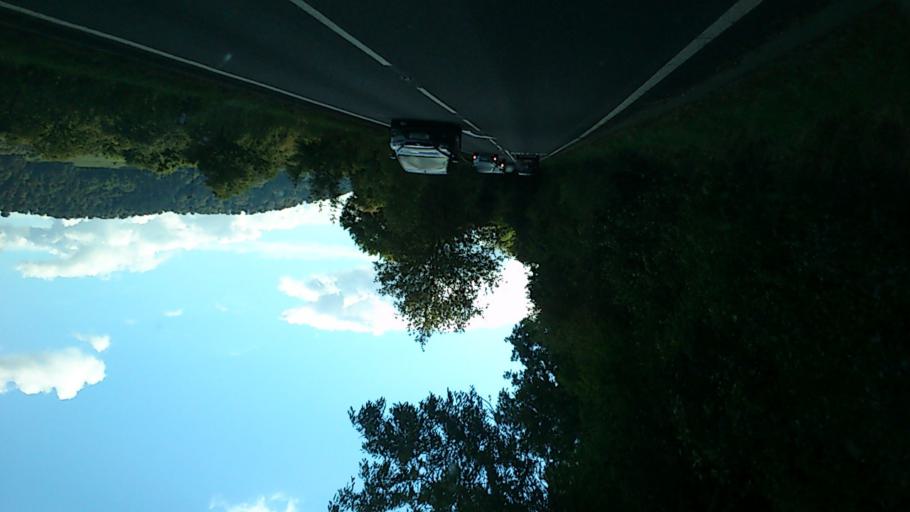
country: GB
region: Wales
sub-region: Sir Powys
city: Welshpool
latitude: 52.6850
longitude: -3.0869
